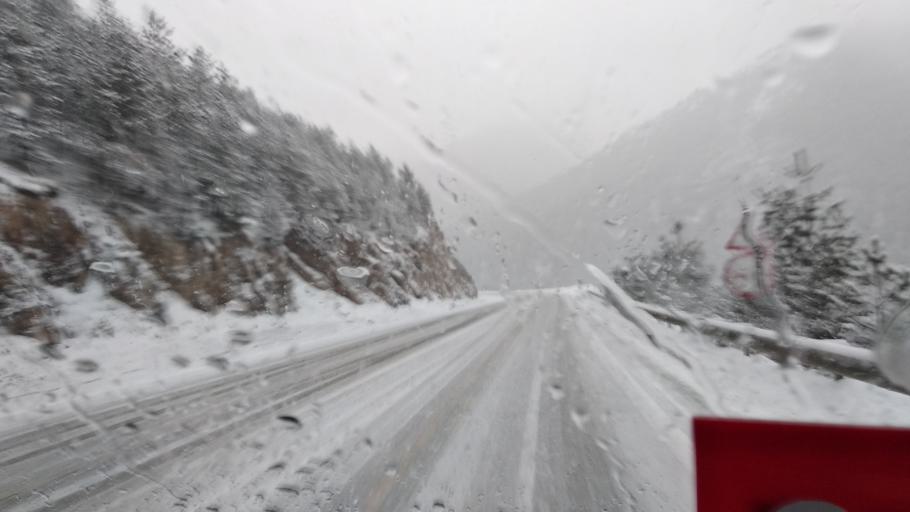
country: TR
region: Gumushane
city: Yaglidere
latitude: 40.6573
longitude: 39.4101
